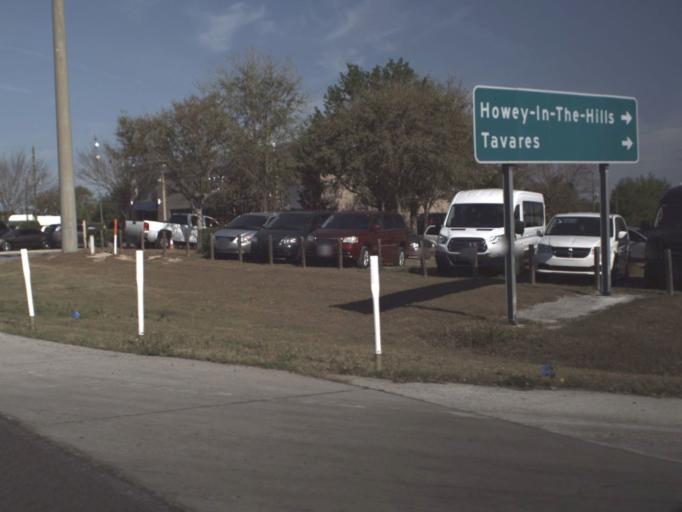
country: US
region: Florida
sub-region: Lake County
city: Howie In The Hills
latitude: 28.6416
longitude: -81.8015
